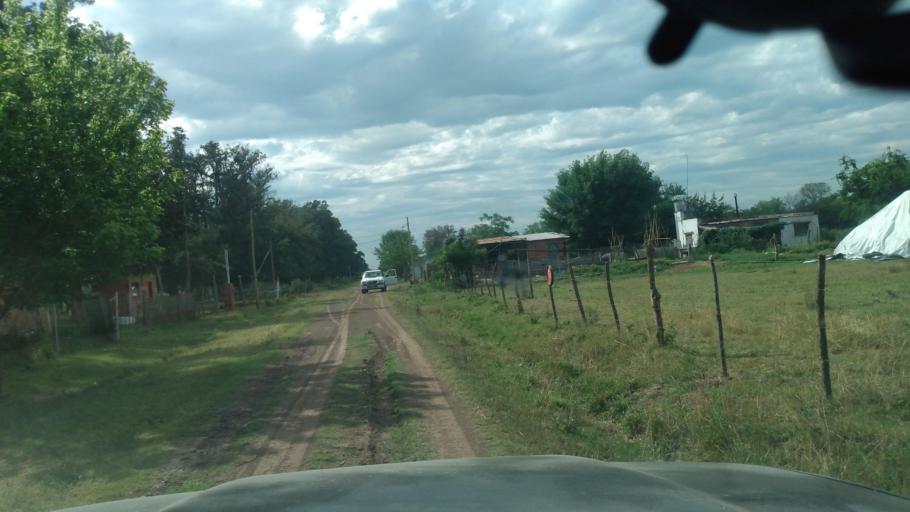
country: AR
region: Buenos Aires
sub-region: Partido de Lujan
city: Lujan
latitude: -34.5989
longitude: -59.0590
